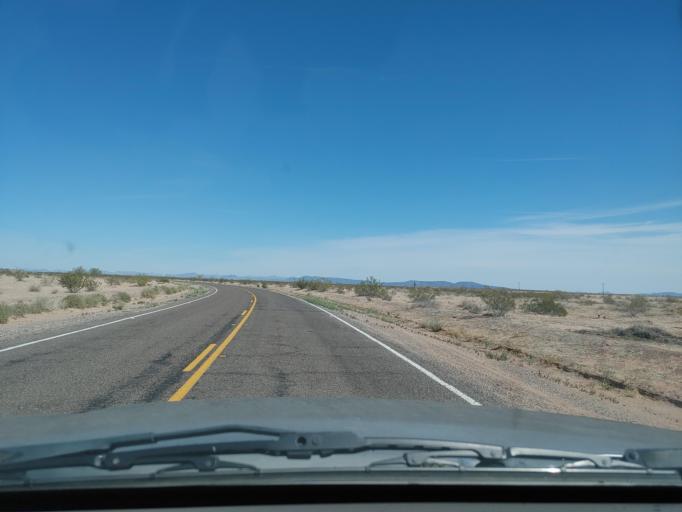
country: US
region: Arizona
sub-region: Maricopa County
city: Gila Bend
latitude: 32.8694
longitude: -113.2129
